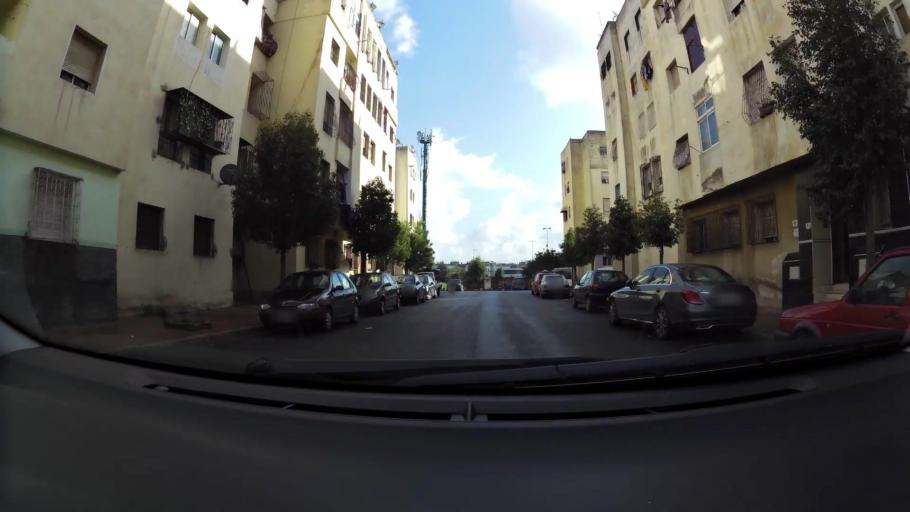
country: MA
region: Grand Casablanca
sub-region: Mediouna
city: Tit Mellil
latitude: 33.5952
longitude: -7.5337
